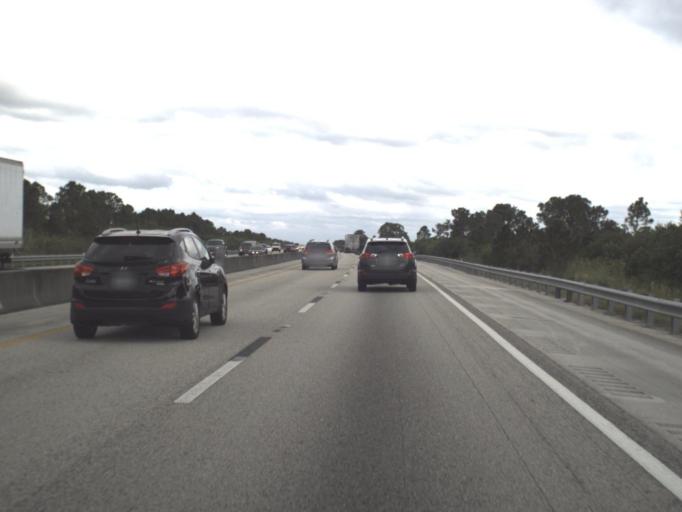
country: US
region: Florida
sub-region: Martin County
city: Hobe Sound
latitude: 27.0271
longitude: -80.2333
